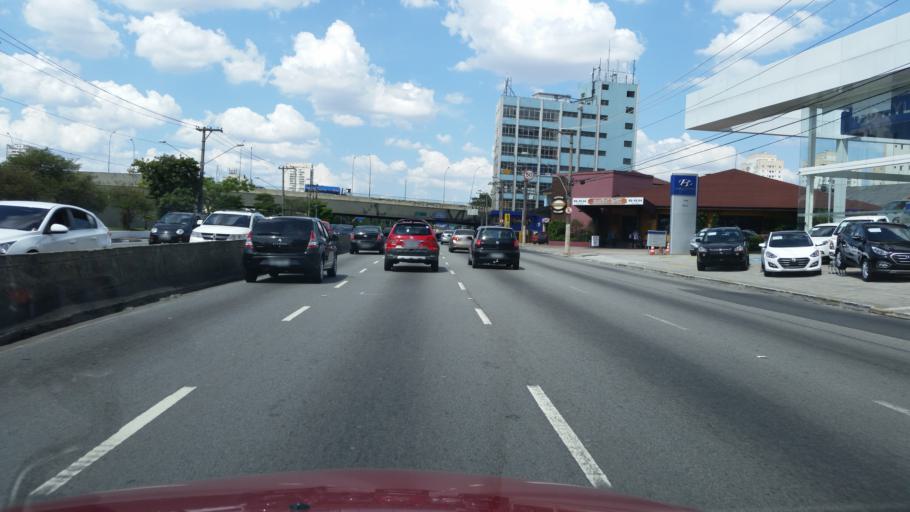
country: BR
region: Sao Paulo
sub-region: Sao Paulo
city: Sao Paulo
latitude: -23.5449
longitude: -46.5949
